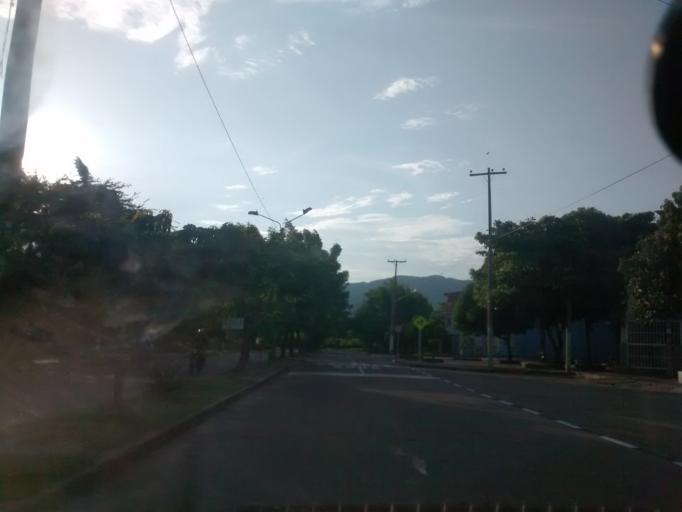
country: CO
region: Tolima
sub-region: Flandes
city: Flandes
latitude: 4.2929
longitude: -74.8213
